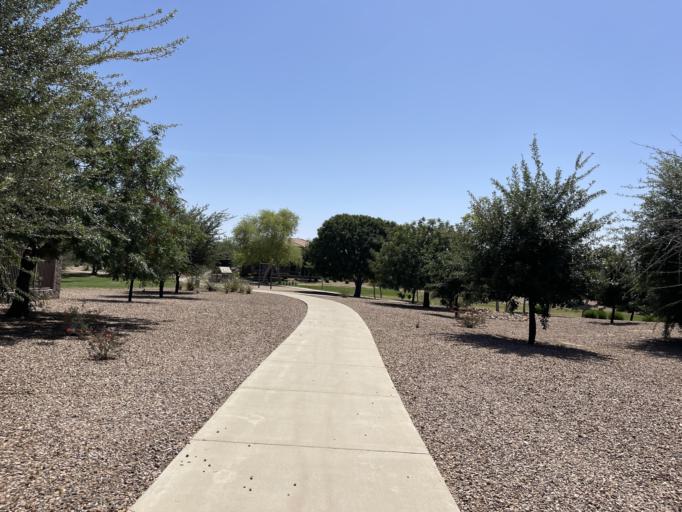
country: US
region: Arizona
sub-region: Maricopa County
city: Queen Creek
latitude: 33.2774
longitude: -111.6957
